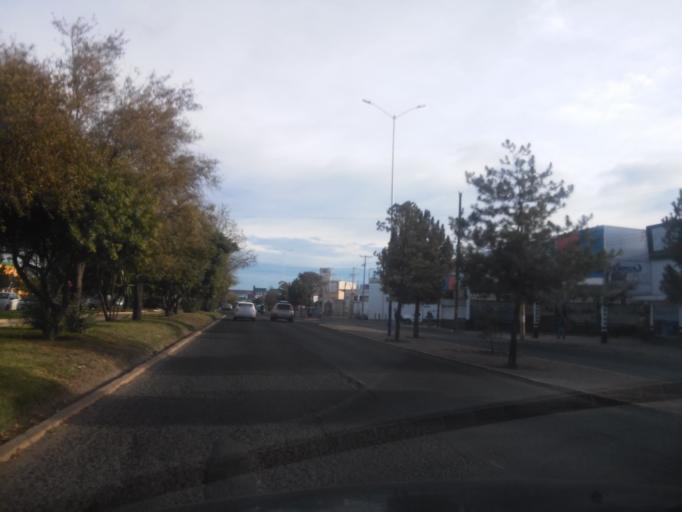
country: MX
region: Durango
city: Victoria de Durango
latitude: 24.0390
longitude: -104.6324
